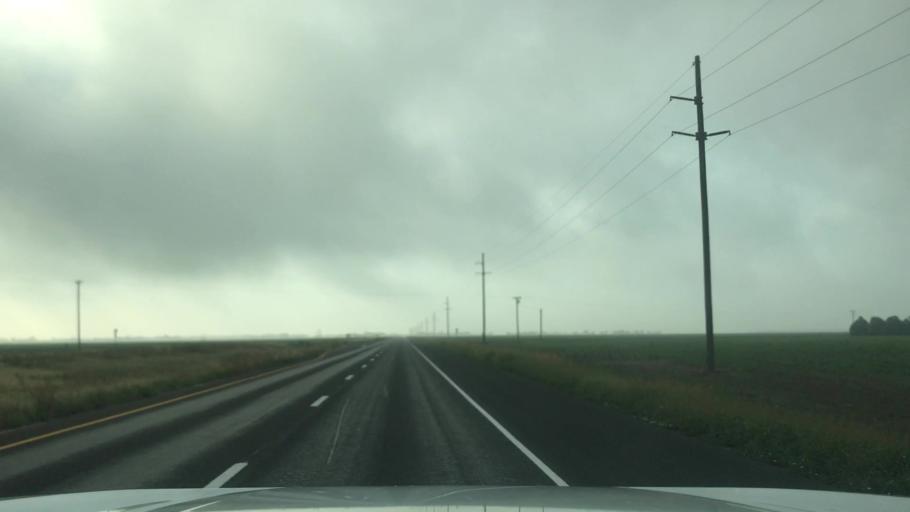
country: US
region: Texas
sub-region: Lubbock County
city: Slaton
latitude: 33.3727
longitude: -101.5746
